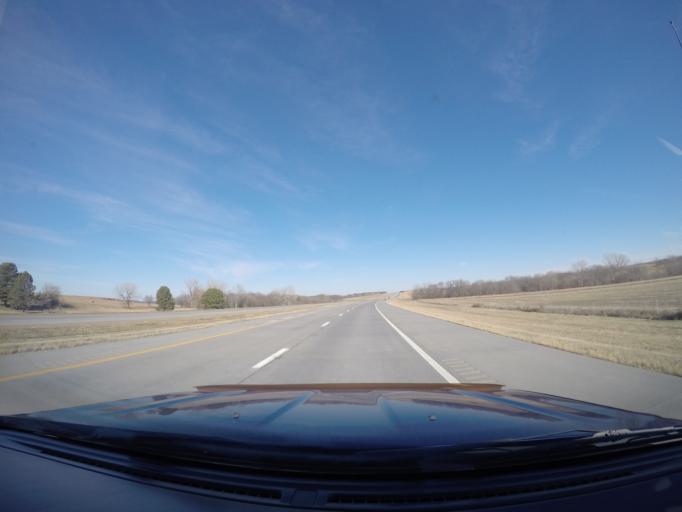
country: US
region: Kansas
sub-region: Republic County
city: Belleville
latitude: 39.7297
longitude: -97.6601
